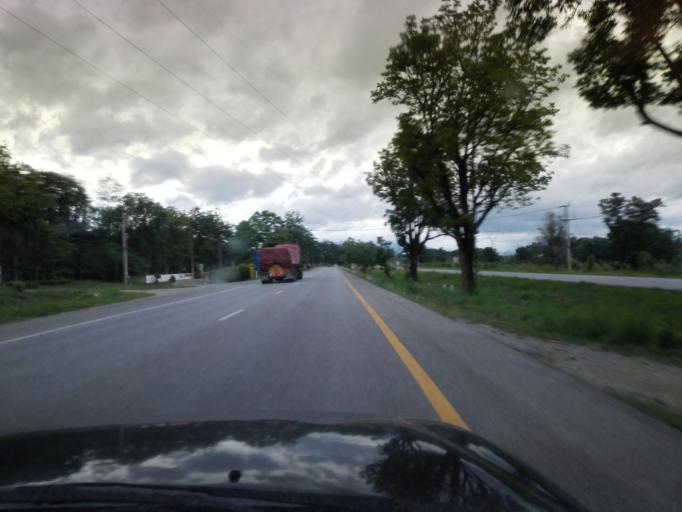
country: TH
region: Tak
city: Tak
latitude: 16.7982
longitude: 99.1531
